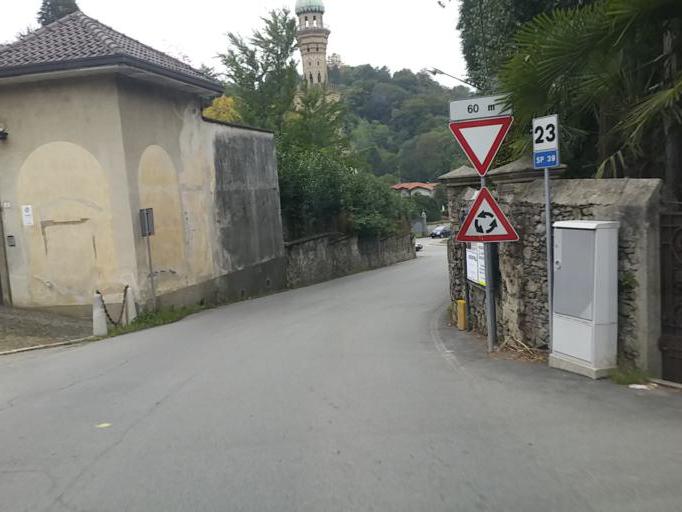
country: IT
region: Piedmont
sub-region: Provincia di Novara
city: Orta San Giulio
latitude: 45.7959
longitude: 8.4178
